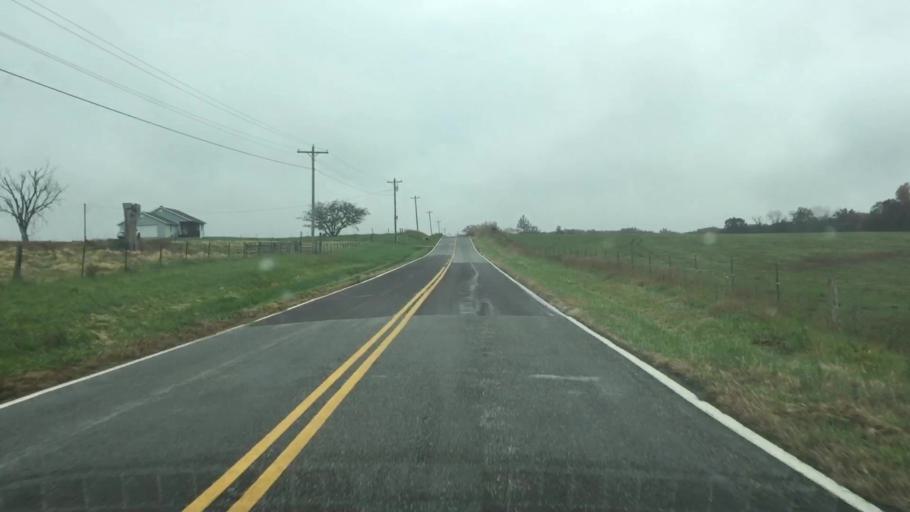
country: US
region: Missouri
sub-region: Callaway County
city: Fulton
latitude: 38.8303
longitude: -91.9166
